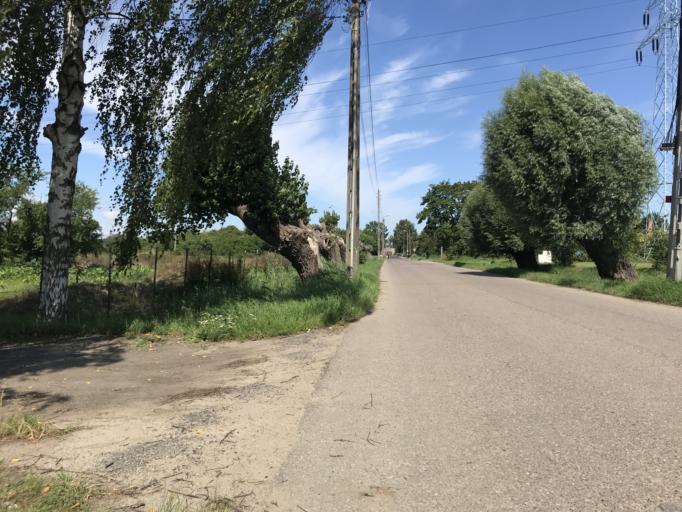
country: PL
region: Pomeranian Voivodeship
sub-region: Gdansk
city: Gdansk
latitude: 54.3334
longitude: 18.6792
